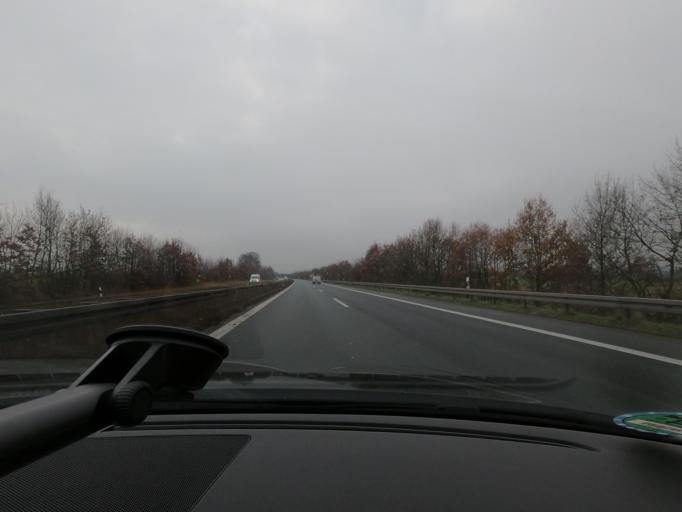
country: DE
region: Bavaria
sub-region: Upper Franconia
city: Altendorf
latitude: 49.8144
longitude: 11.0113
